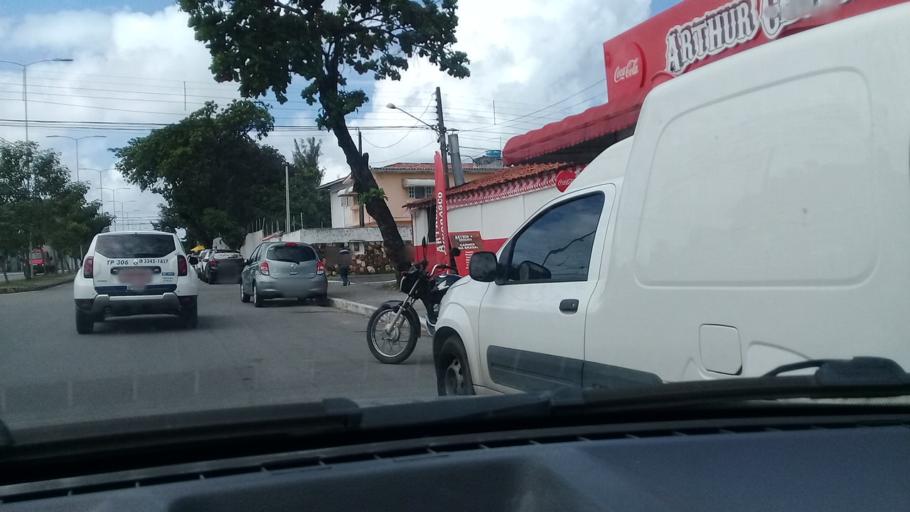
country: BR
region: Pernambuco
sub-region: Jaboatao Dos Guararapes
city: Jaboatao
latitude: -8.1637
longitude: -34.9190
